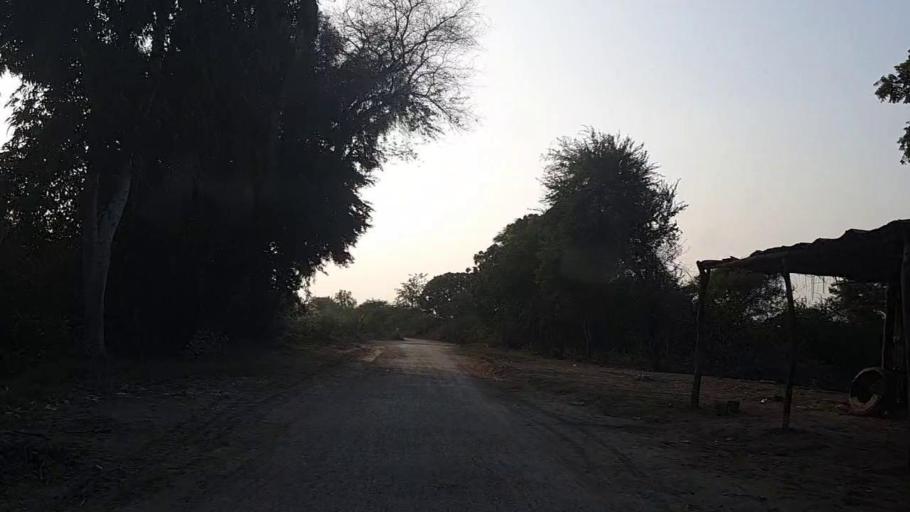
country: PK
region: Sindh
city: Mirpur Sakro
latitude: 24.5586
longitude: 67.5890
